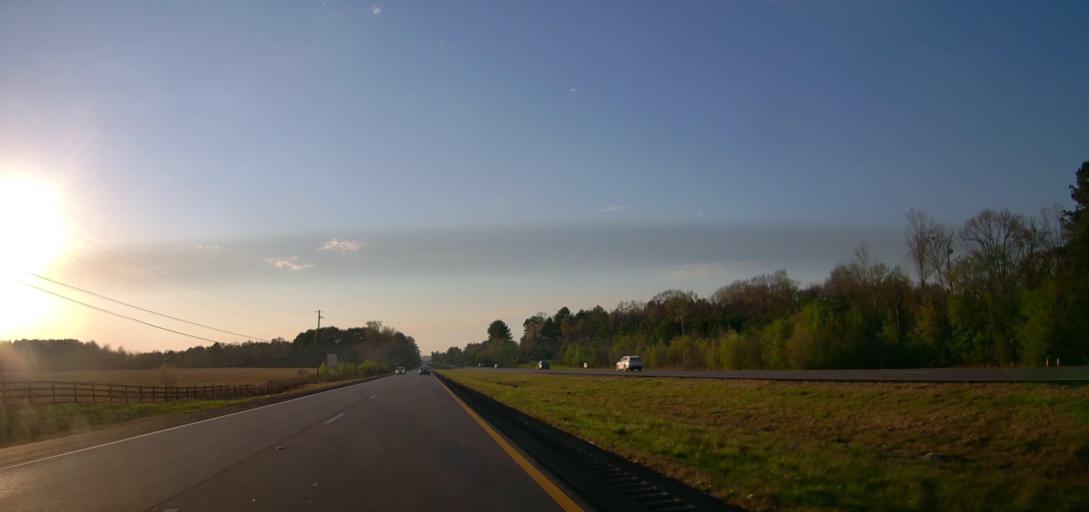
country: US
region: Alabama
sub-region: Shelby County
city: Harpersville
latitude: 33.3260
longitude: -86.4088
